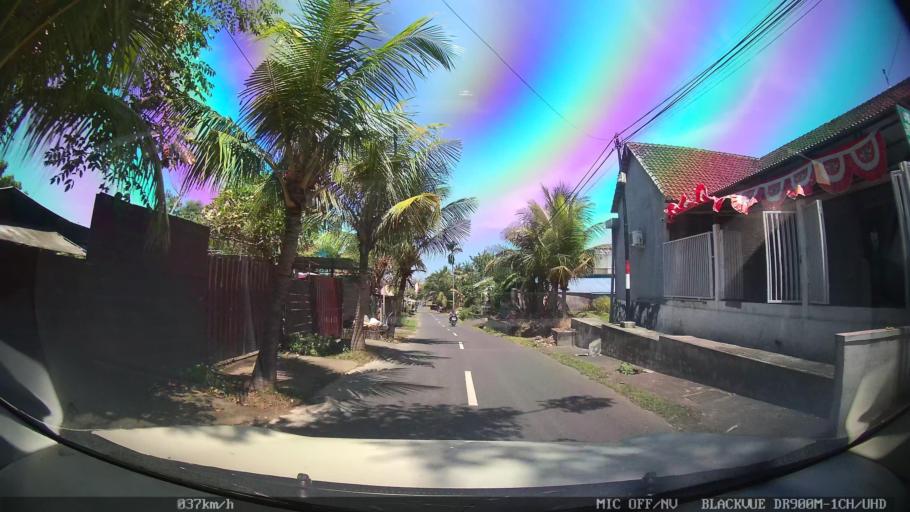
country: ID
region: Bali
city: Banjar Pasekan
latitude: -8.5657
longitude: 115.3202
